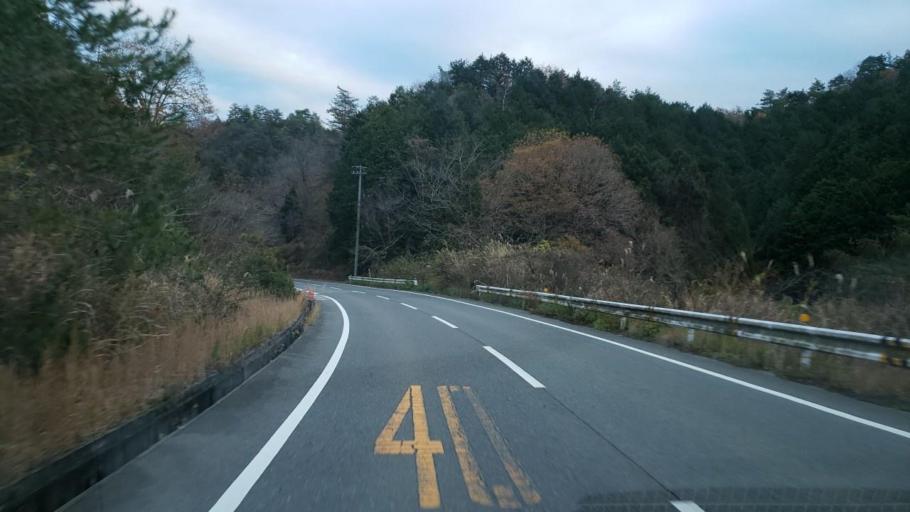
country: JP
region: Tokushima
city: Wakimachi
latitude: 34.1795
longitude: 134.1821
